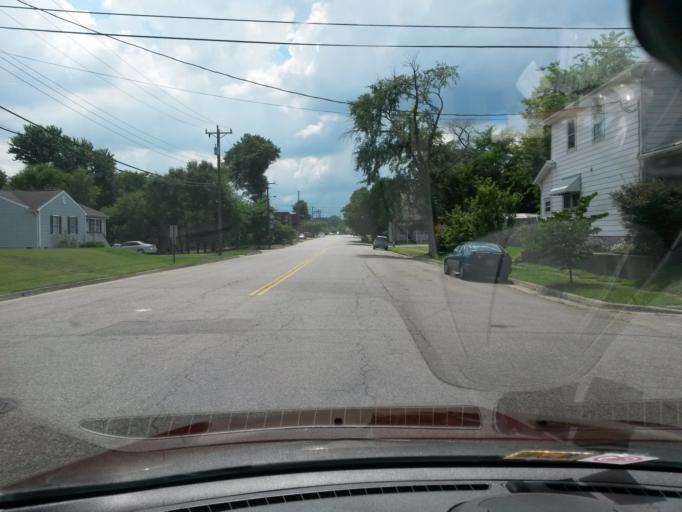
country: US
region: Virginia
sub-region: City of Hopewell
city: Hopewell
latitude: 37.3079
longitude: -77.2832
